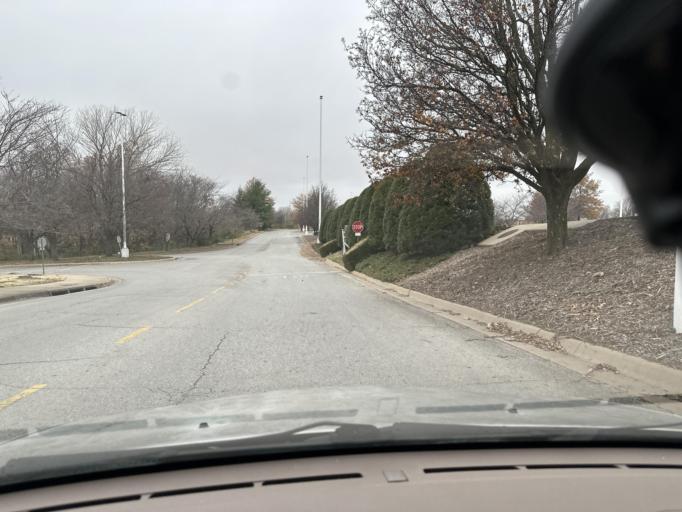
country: US
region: Arkansas
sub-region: Washington County
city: Johnson
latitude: 36.1261
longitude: -94.1492
